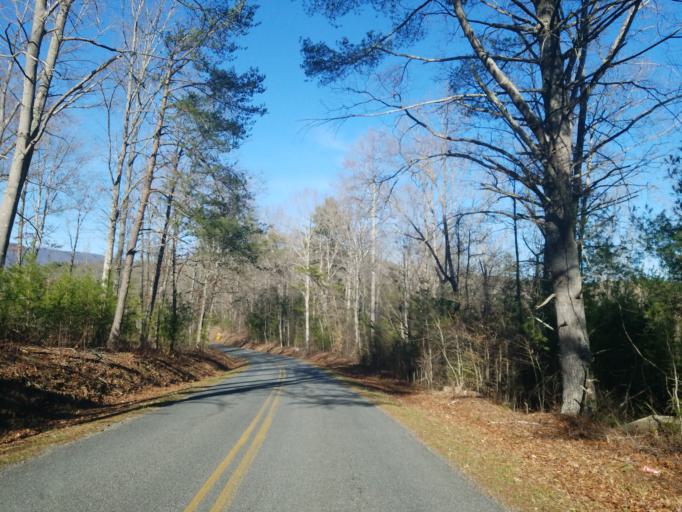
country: US
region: Georgia
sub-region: Gilmer County
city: Ellijay
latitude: 34.6334
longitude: -84.3708
